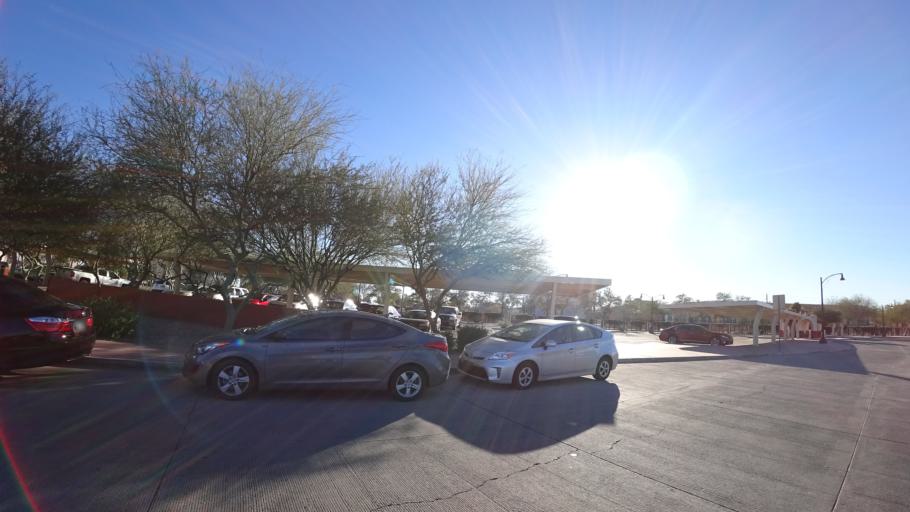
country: US
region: Arizona
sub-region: Maricopa County
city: Gilbert
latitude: 33.3549
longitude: -111.7914
